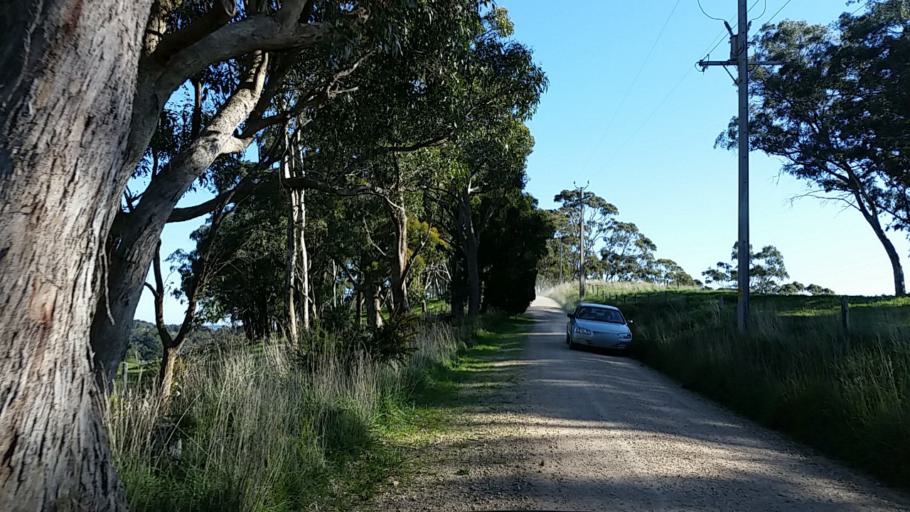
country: AU
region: South Australia
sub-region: Adelaide Hills
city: Lobethal
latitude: -34.8821
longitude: 138.8681
